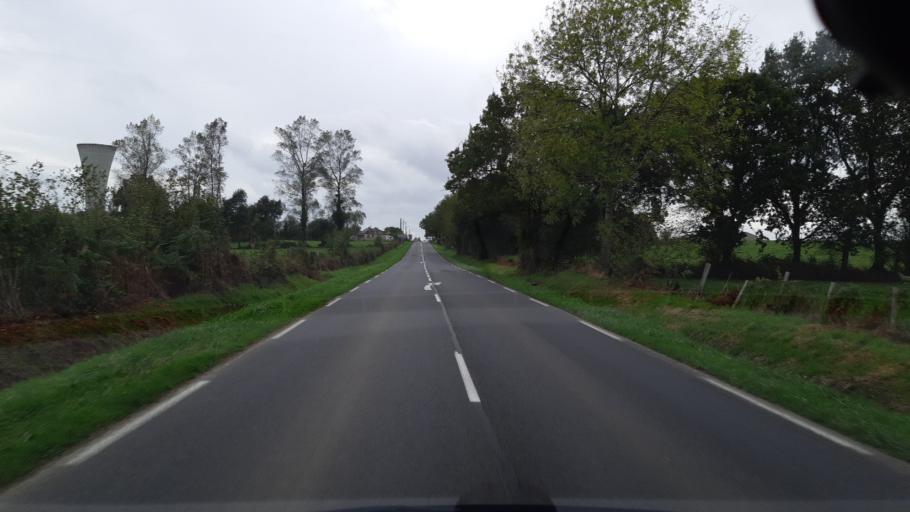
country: FR
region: Lower Normandy
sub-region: Departement de la Manche
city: Gavray
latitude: 48.9349
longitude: -1.3735
